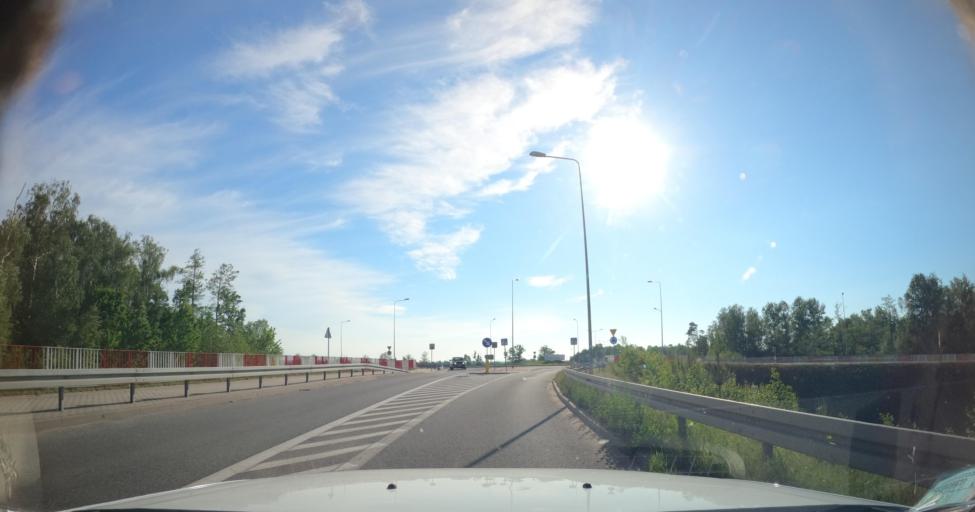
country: PL
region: Warmian-Masurian Voivodeship
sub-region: Powiat elblaski
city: Paslek
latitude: 54.0813
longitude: 19.6113
